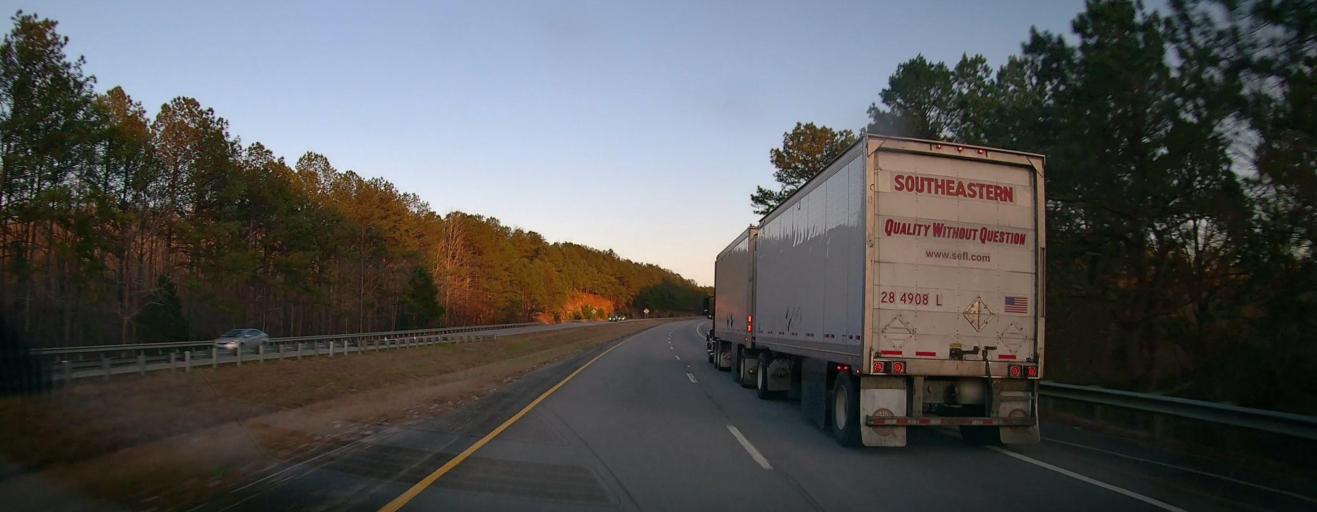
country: US
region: Alabama
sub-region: Coosa County
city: Goodwater
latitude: 33.0361
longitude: -86.1226
